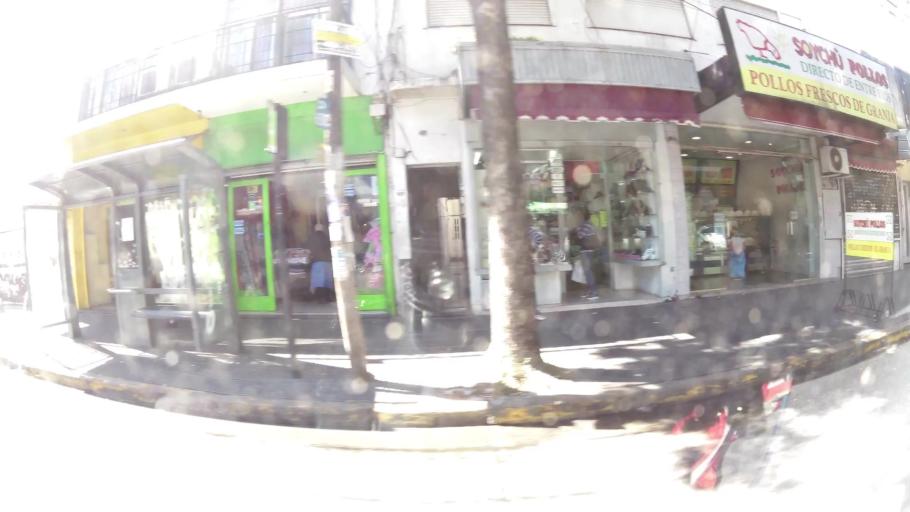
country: AR
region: Buenos Aires
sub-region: Partido de General San Martin
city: General San Martin
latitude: -34.5302
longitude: -58.5237
